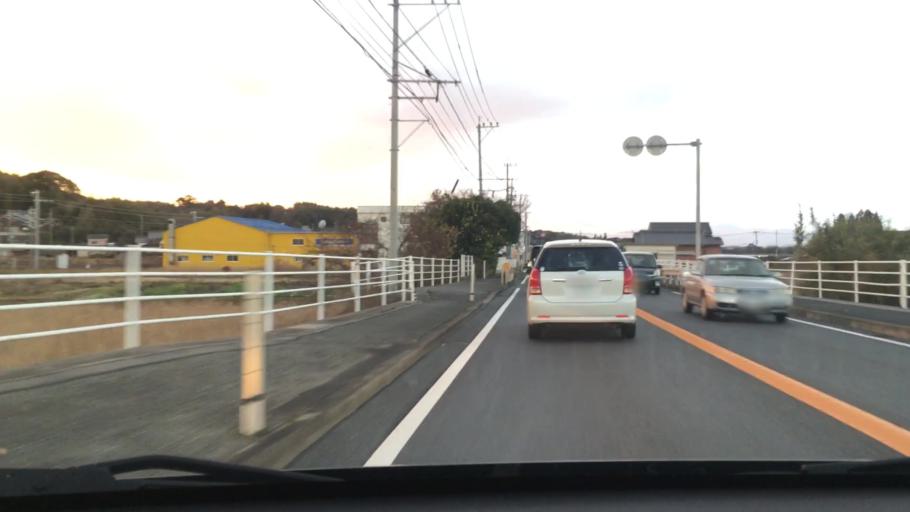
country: JP
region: Fukuoka
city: Shiida
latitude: 33.6316
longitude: 131.0818
